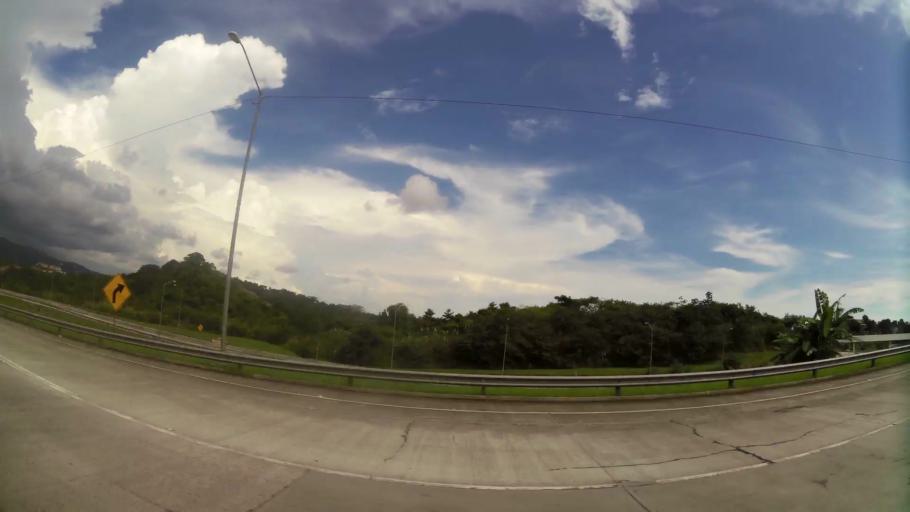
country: PA
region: Panama
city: San Miguelito
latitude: 9.0750
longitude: -79.4805
